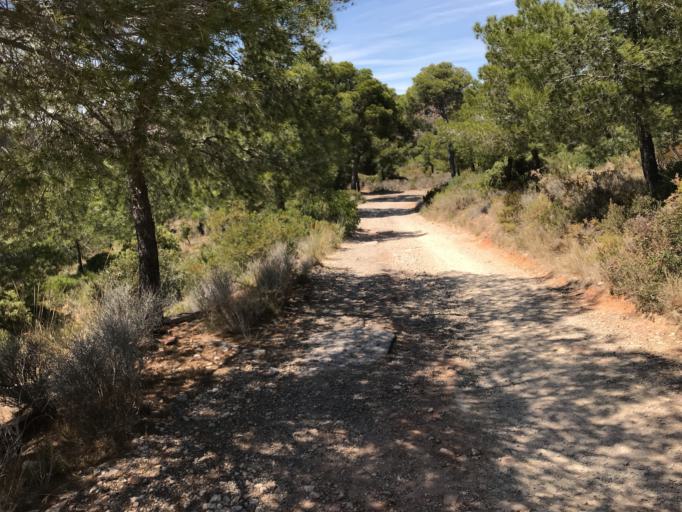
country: ES
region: Valencia
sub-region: Provincia de Valencia
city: Pucol
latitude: 39.6445
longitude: -0.3211
